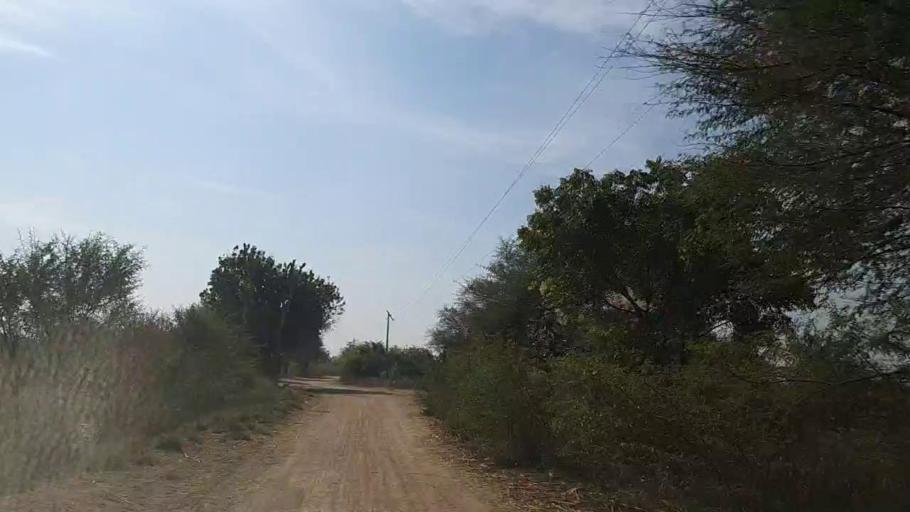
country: PK
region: Sindh
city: Mirpur Khas
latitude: 25.4735
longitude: 68.9745
